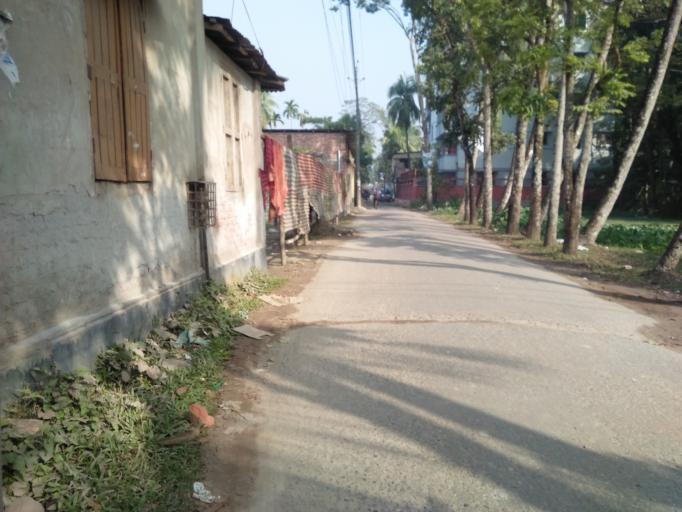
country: BD
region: Barisal
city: Bhola
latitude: 22.6809
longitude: 90.6425
